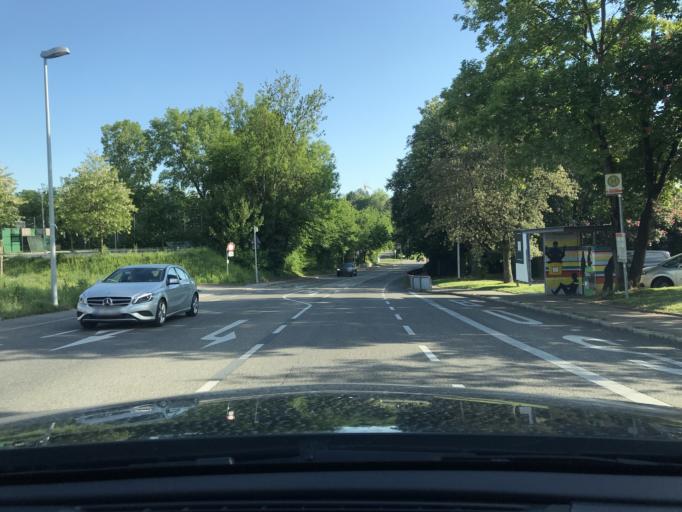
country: DE
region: Baden-Wuerttemberg
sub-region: Regierungsbezirk Stuttgart
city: Waiblingen
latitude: 48.8539
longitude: 9.3268
